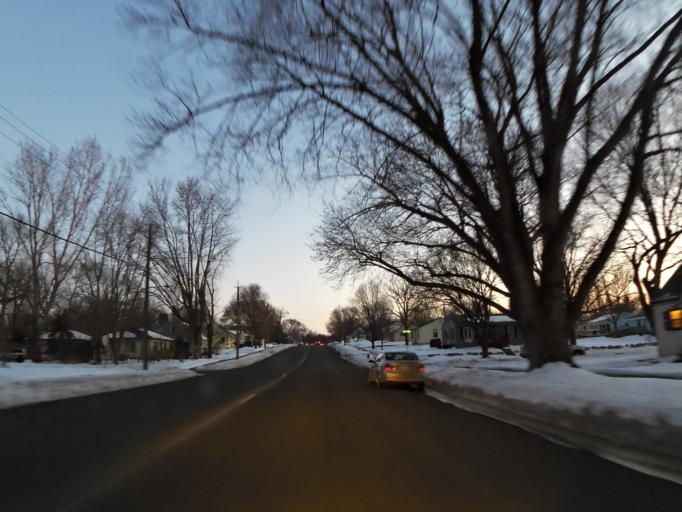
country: US
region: Minnesota
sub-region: Scott County
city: Shakopee
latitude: 44.7924
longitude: -93.5208
